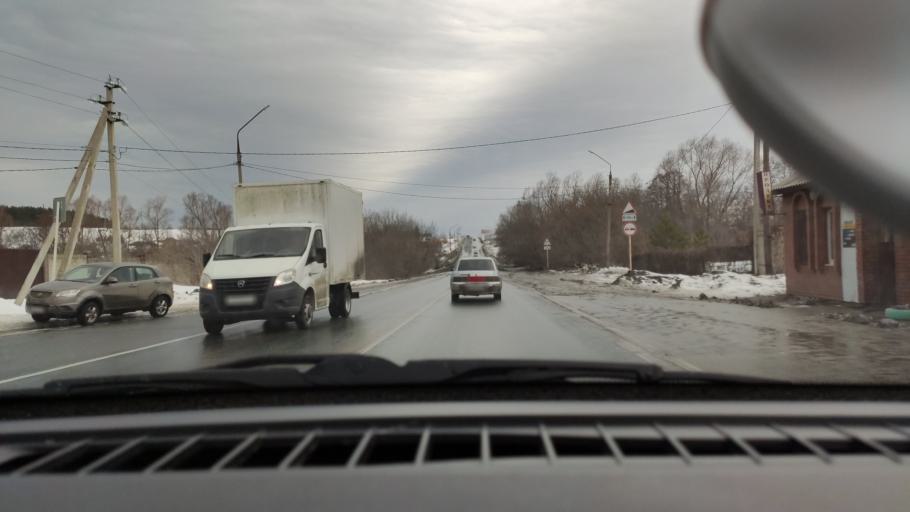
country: RU
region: Samara
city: Kurumoch
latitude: 53.4820
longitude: 50.0451
